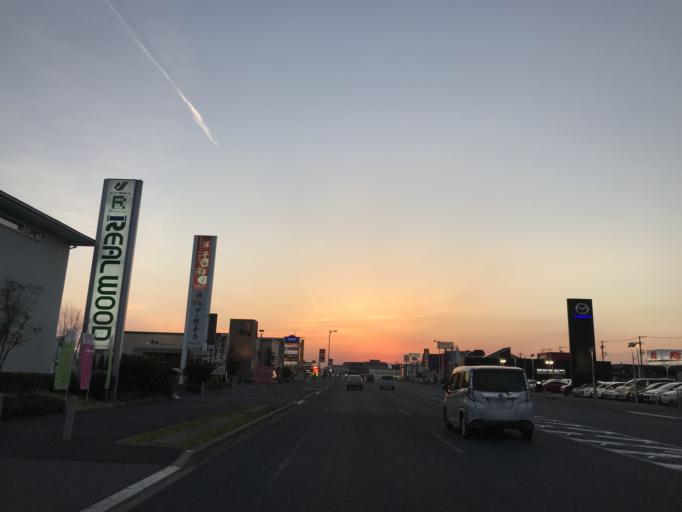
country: JP
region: Ibaraki
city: Naka
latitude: 36.0849
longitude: 140.0781
